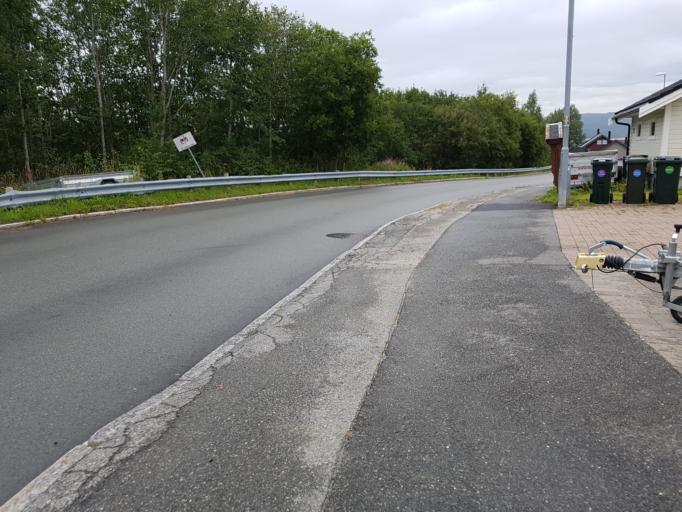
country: NO
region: Sor-Trondelag
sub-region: Trondheim
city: Trondheim
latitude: 63.3854
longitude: 10.3408
